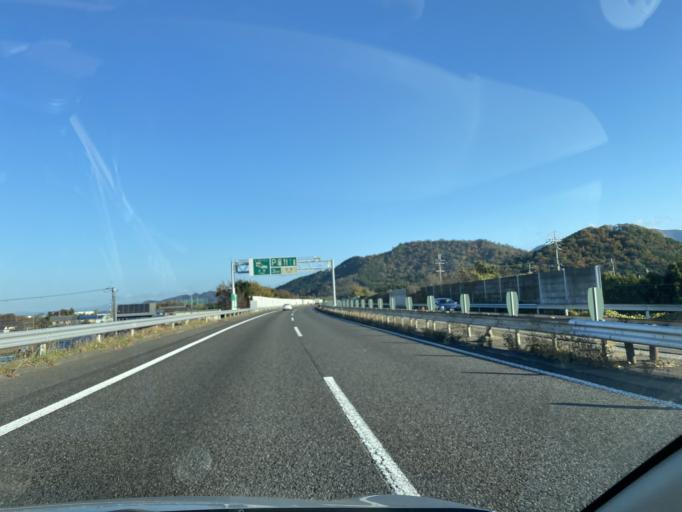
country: JP
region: Shiga Prefecture
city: Hikone
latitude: 35.1962
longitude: 136.2820
